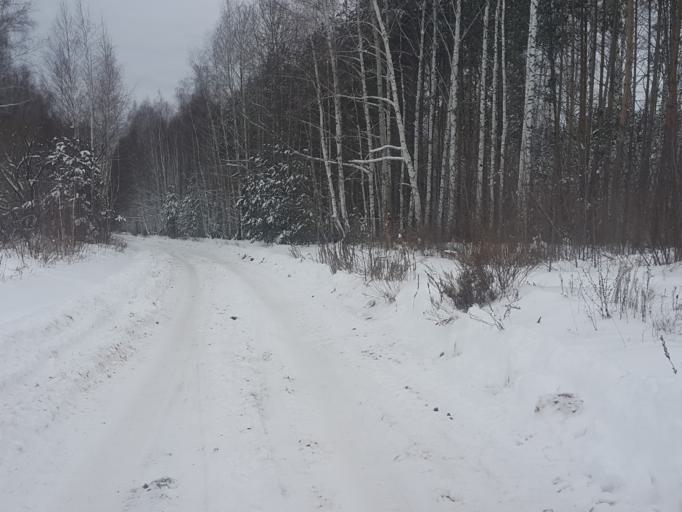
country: RU
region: Tambov
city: Platonovka
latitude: 52.8901
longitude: 41.8511
